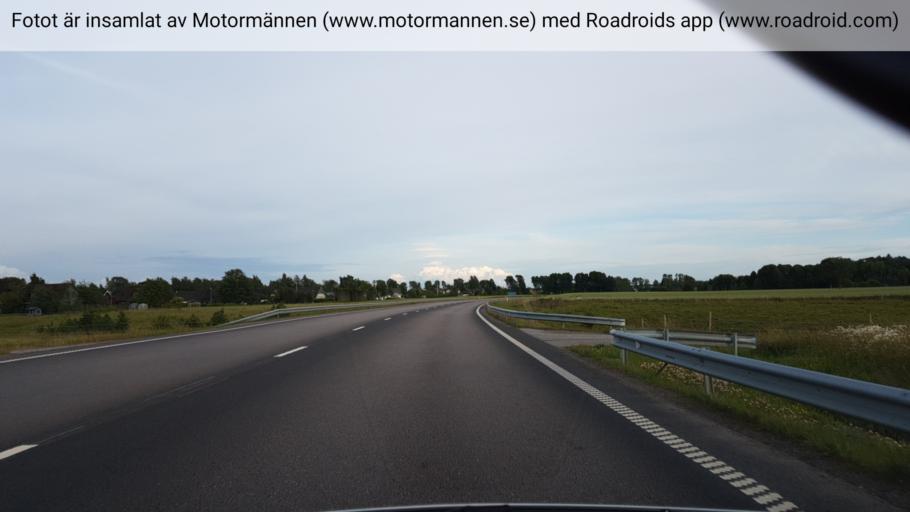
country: SE
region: Vaestra Goetaland
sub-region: Skara Kommun
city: Skara
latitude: 58.3931
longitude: 13.4083
